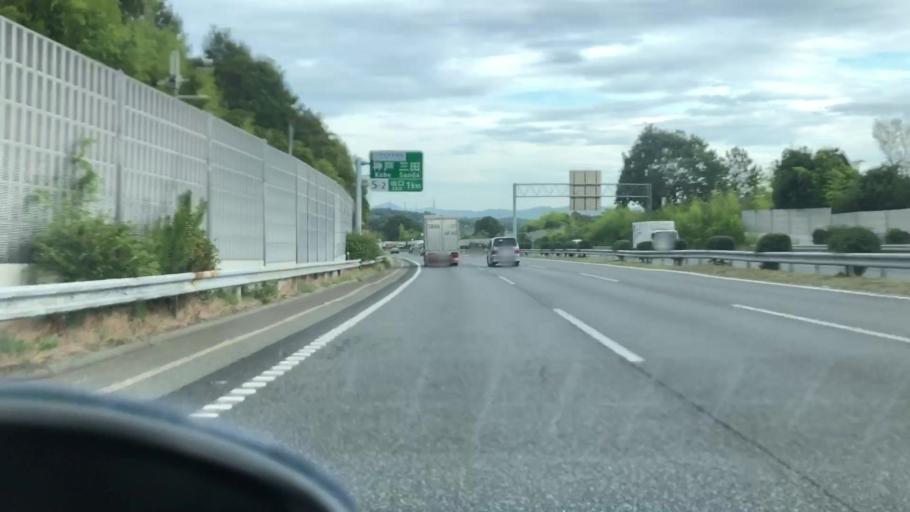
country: JP
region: Hyogo
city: Sandacho
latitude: 34.8847
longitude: 135.1739
